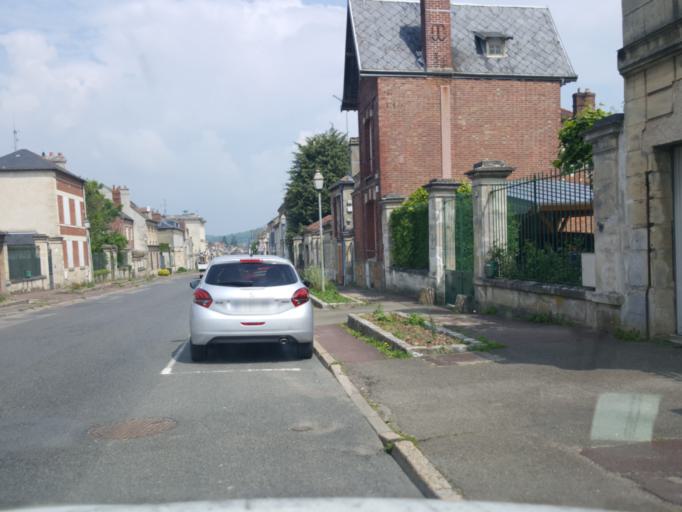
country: FR
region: Ile-de-France
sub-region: Departement du Val-d'Oise
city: Magny-en-Vexin
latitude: 49.1499
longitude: 1.7882
